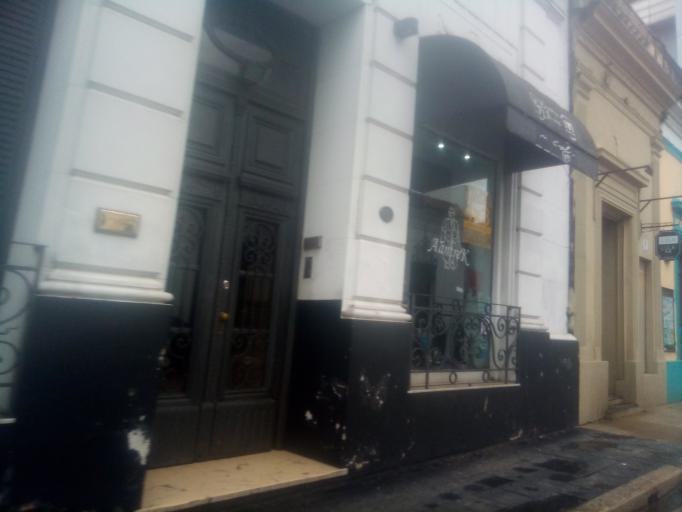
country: AR
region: Corrientes
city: Corrientes
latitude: -27.4664
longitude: -58.8375
